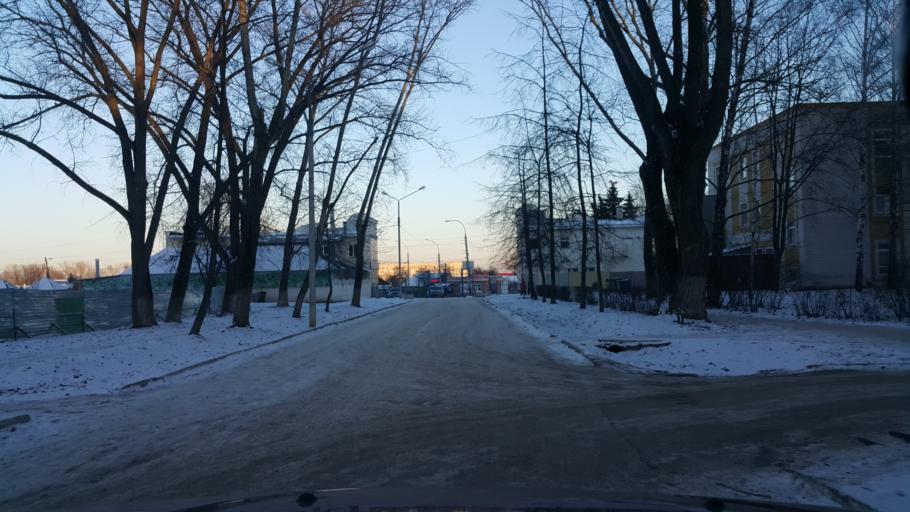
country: RU
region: Tambov
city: Pokrovo-Prigorodnoye
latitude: 52.7097
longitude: 41.3952
